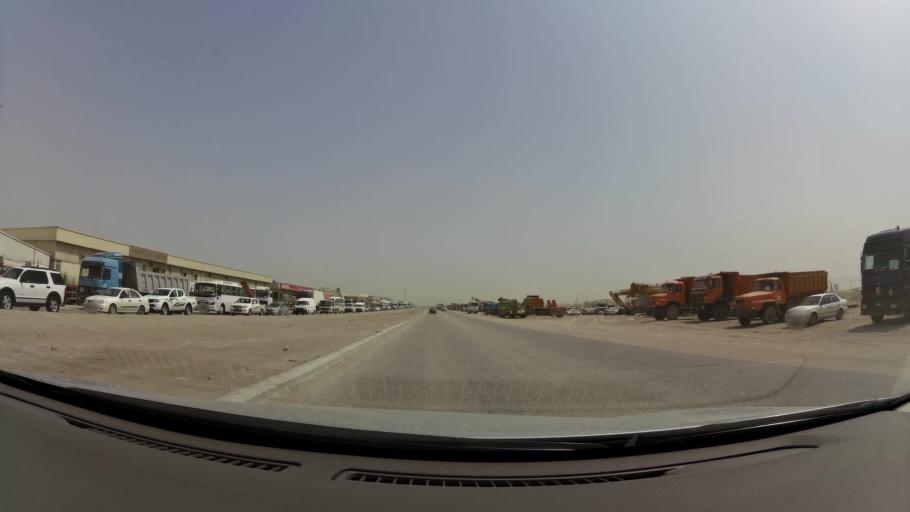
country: QA
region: Baladiyat ar Rayyan
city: Ar Rayyan
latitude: 25.1844
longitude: 51.4306
